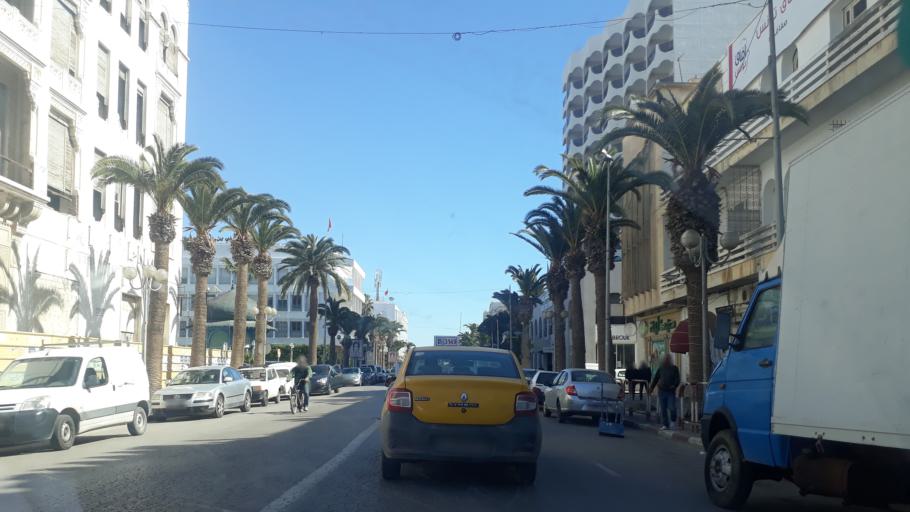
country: TN
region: Safaqis
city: Sfax
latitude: 34.7329
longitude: 10.7643
